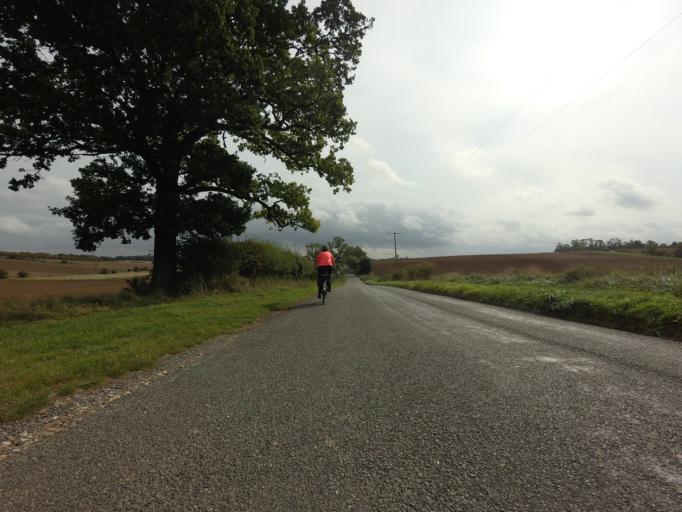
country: GB
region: England
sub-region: Essex
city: Saffron Walden
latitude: 52.0278
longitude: 0.1814
